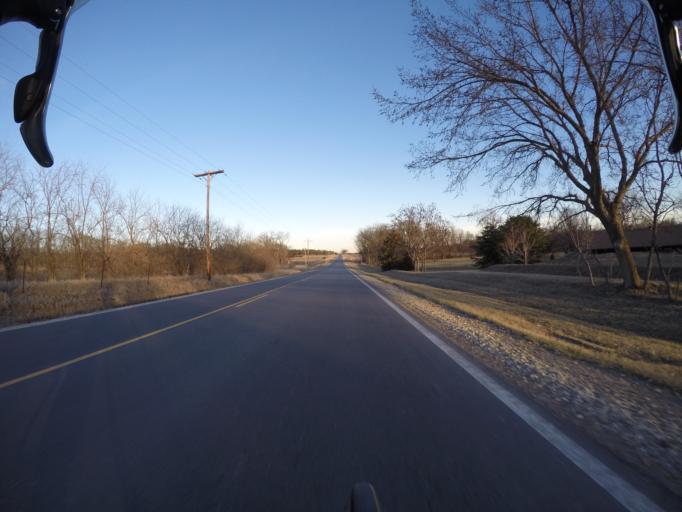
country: US
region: Kansas
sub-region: Riley County
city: Ogden
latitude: 39.2118
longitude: -96.6815
